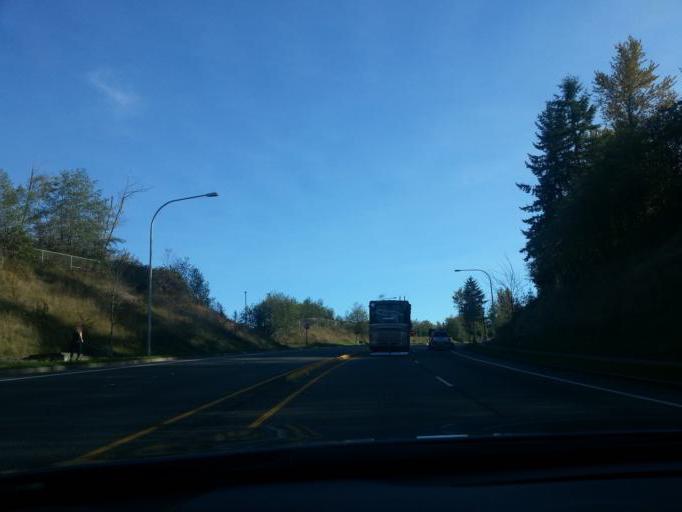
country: US
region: Washington
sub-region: Snohomish County
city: Silver Firs
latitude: 47.8699
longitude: -122.1366
